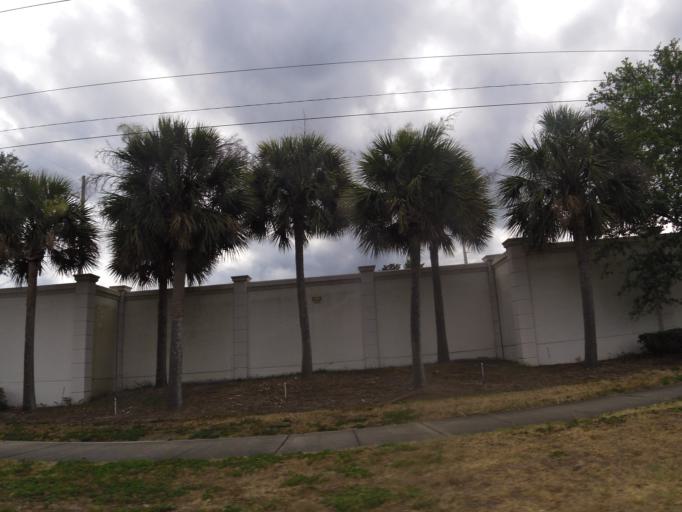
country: US
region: Florida
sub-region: Duval County
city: Jacksonville Beach
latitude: 30.3004
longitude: -81.4066
